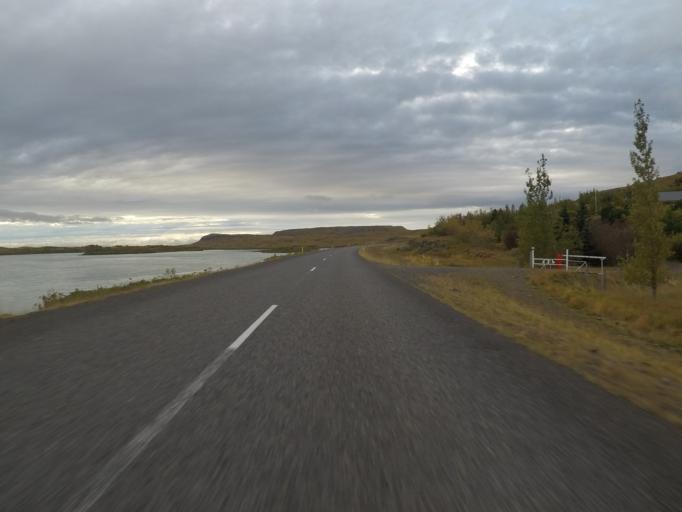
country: IS
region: South
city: Vestmannaeyjar
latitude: 64.0639
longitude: -20.0895
